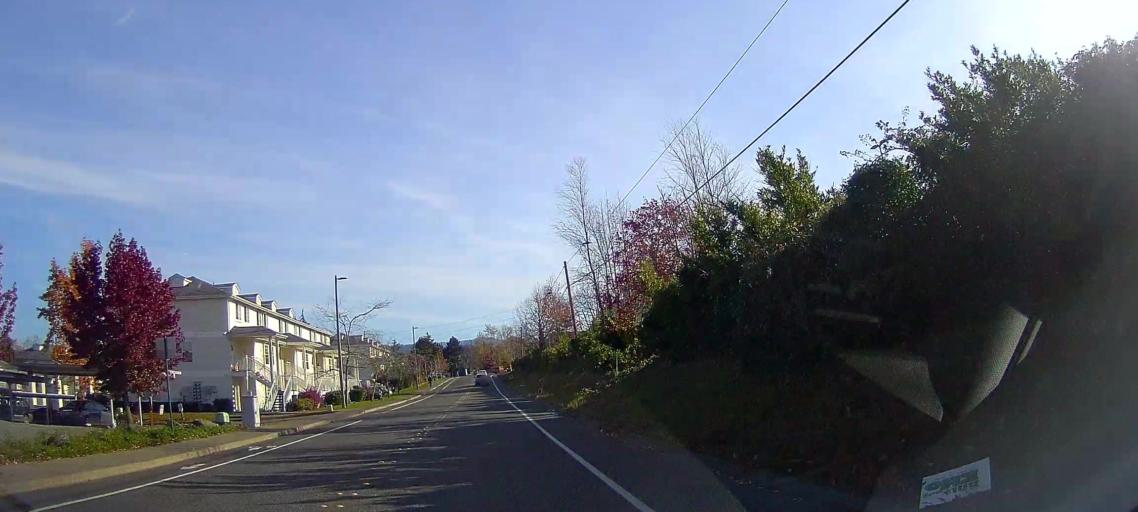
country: US
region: Washington
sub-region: Whatcom County
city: Bellingham
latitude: 48.7751
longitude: -122.4598
